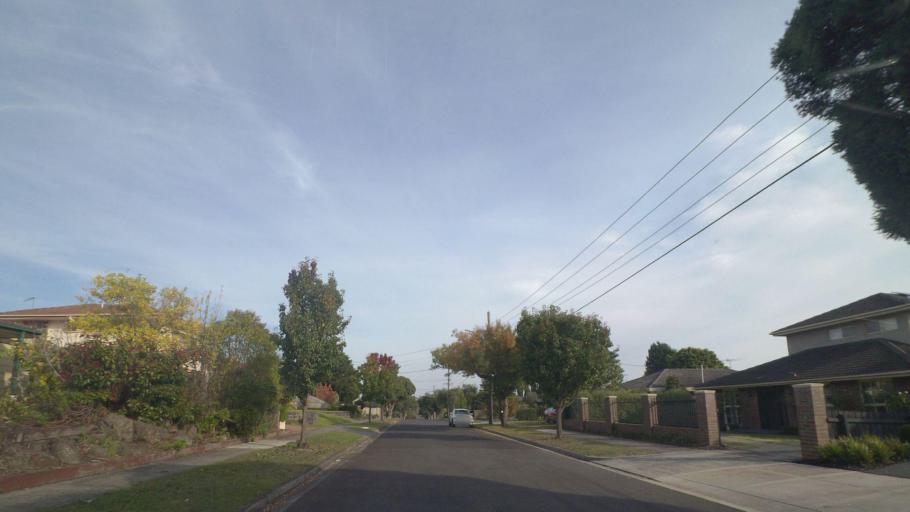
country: AU
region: Victoria
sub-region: Manningham
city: Doncaster East
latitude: -37.7785
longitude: 145.1577
